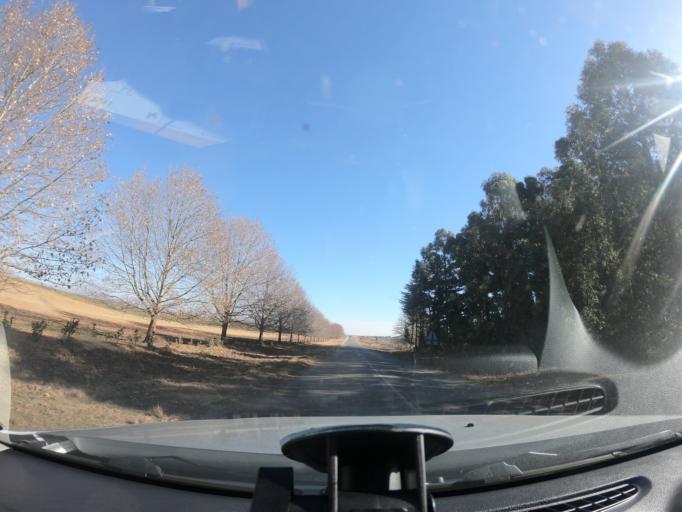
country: ZA
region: KwaZulu-Natal
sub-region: uMgungundlovu District Municipality
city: Mooirivier
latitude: -29.3284
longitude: 29.8425
